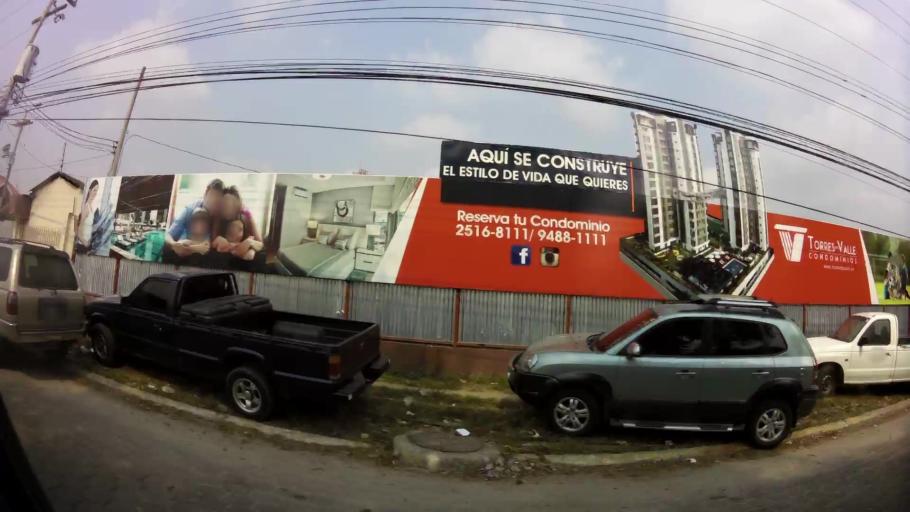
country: HN
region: Cortes
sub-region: San Pedro Sula
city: Pena Blanca
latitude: 15.5346
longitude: -88.0278
